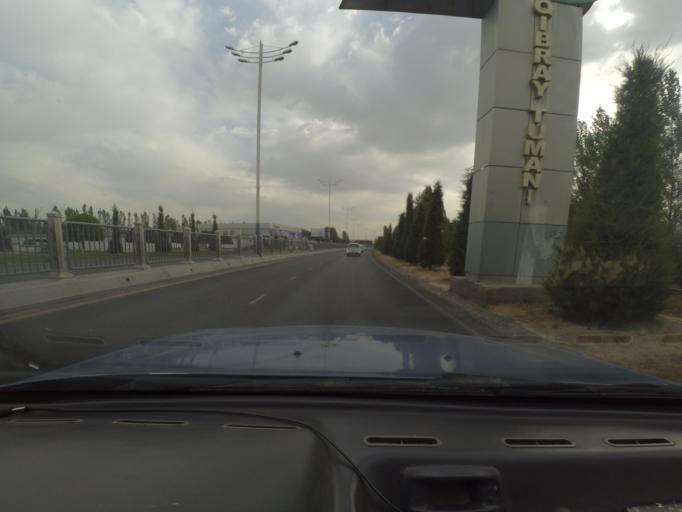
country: UZ
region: Toshkent
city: Salor
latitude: 41.3699
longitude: 69.3972
